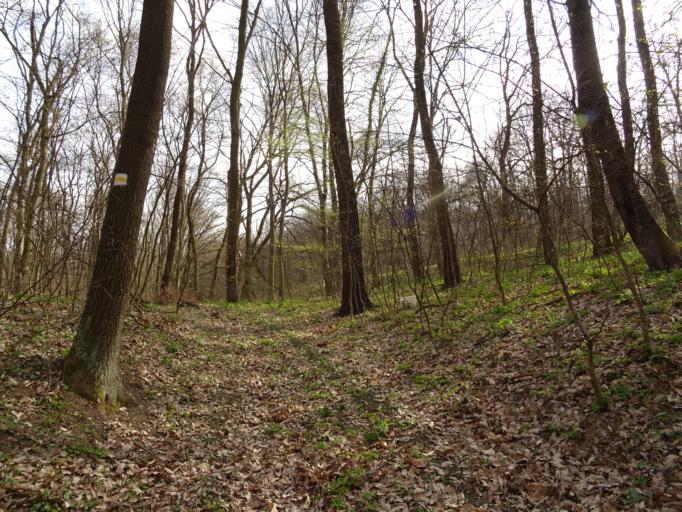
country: HU
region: Fejer
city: Pazmand
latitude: 47.2712
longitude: 18.5969
